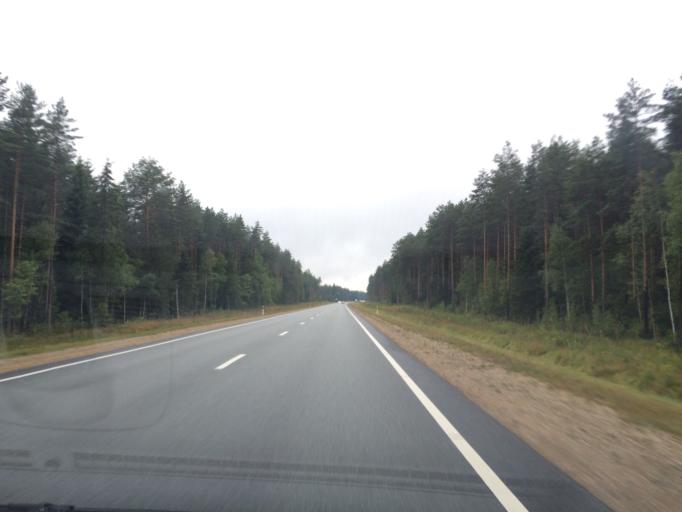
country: LV
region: Ogre
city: Ogre
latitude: 56.8395
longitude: 24.6978
